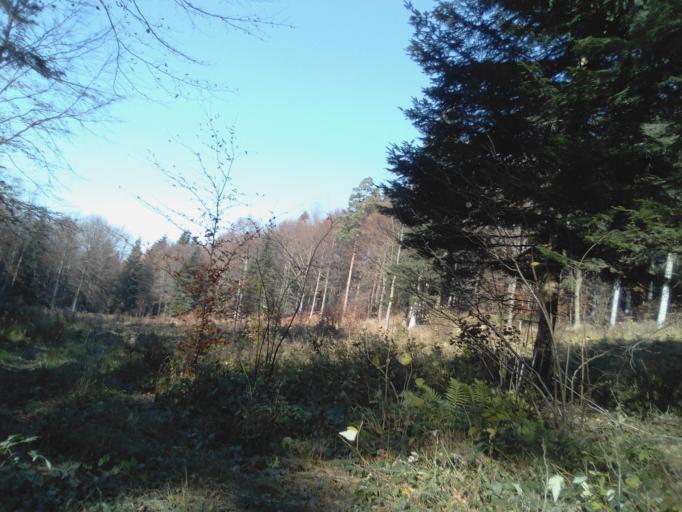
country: PL
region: Subcarpathian Voivodeship
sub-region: Powiat strzyzowski
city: Wisniowa
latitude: 49.8478
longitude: 21.6637
